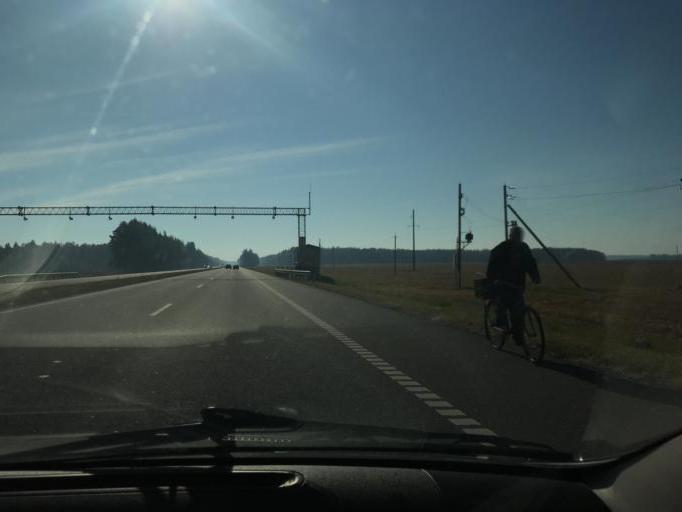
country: BY
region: Minsk
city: Slutsk
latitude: 53.3196
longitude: 27.5351
